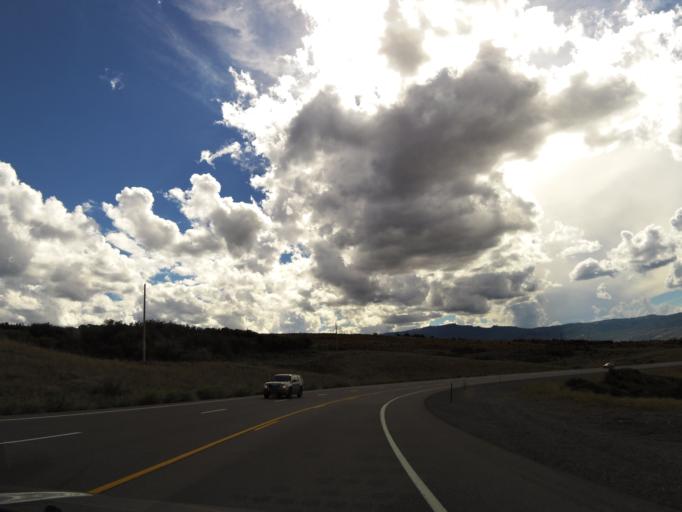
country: US
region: Colorado
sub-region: Hinsdale County
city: Lake City
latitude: 38.3933
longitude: -107.4549
